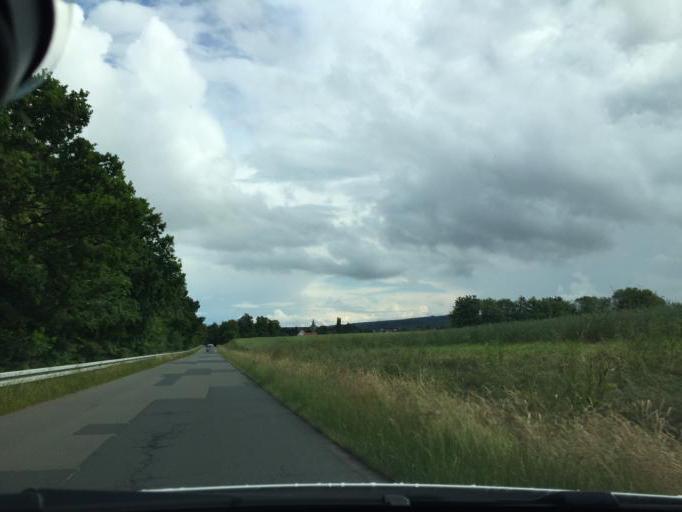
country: DE
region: Lower Saxony
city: Hehlen
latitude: 52.0250
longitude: 9.4151
